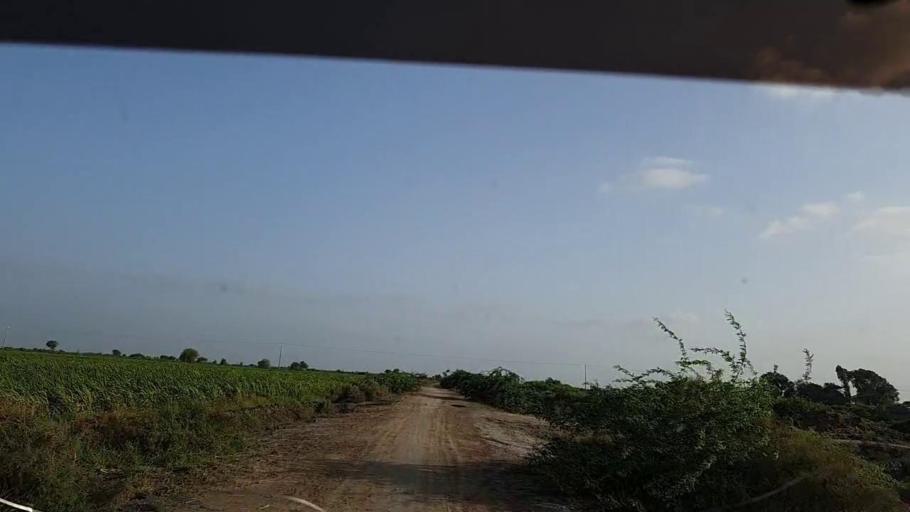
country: PK
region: Sindh
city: Badin
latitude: 24.5545
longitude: 68.8633
